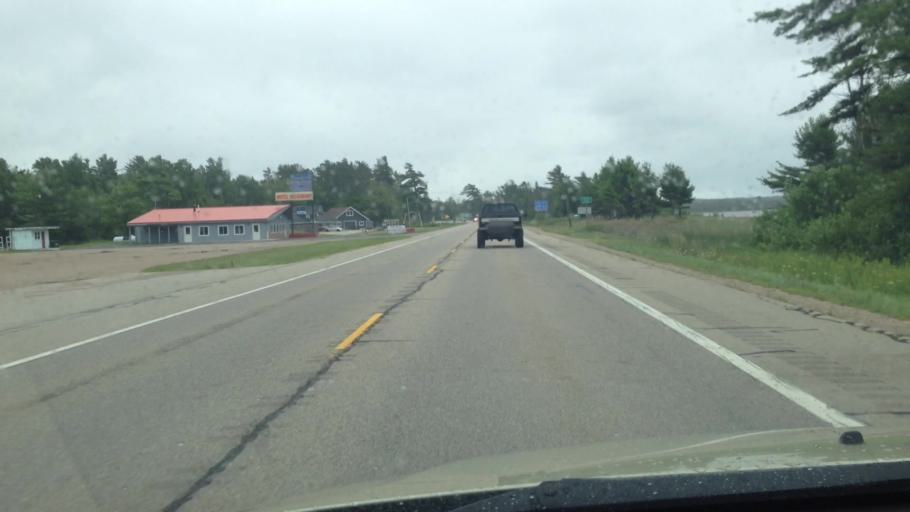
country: US
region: Michigan
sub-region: Schoolcraft County
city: Manistique
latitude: 45.8937
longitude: -86.5464
